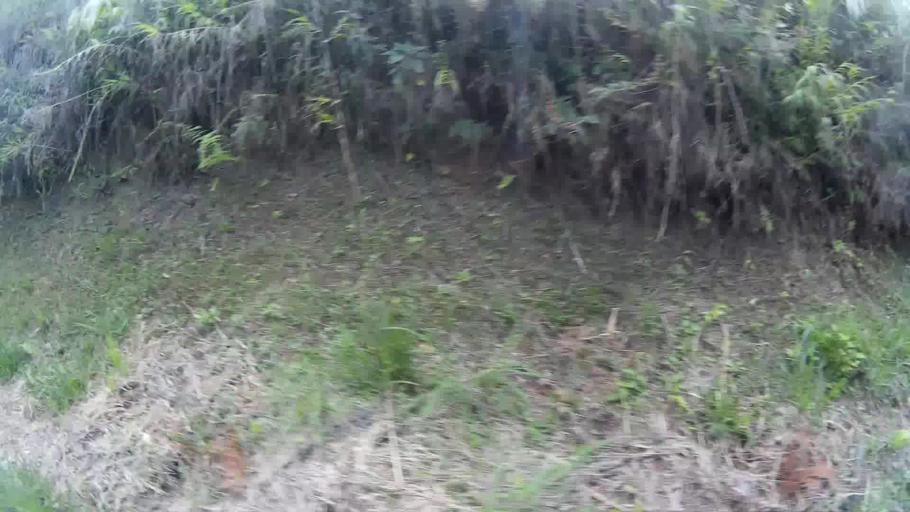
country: CO
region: Valle del Cauca
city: Ulloa
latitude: 4.7274
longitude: -75.7133
